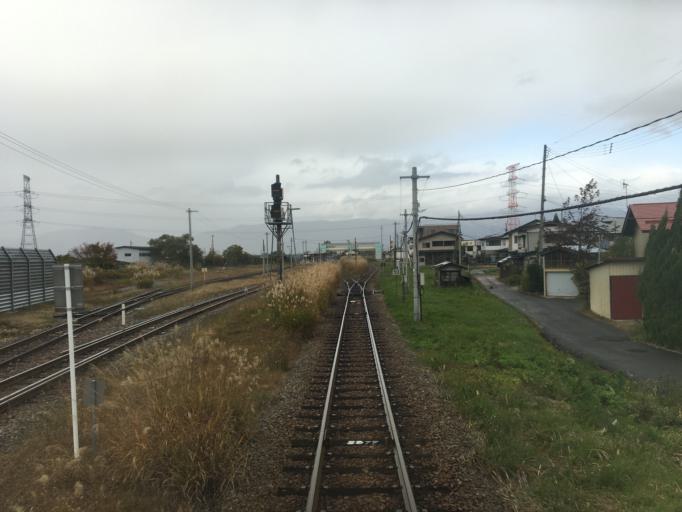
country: JP
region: Yamagata
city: Nagai
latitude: 38.0552
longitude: 140.0459
